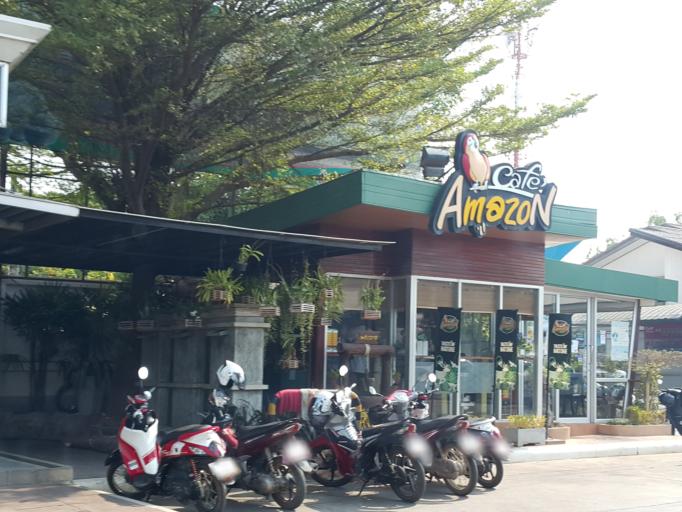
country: TH
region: Sukhothai
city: Sukhothai
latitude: 17.0098
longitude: 99.8029
